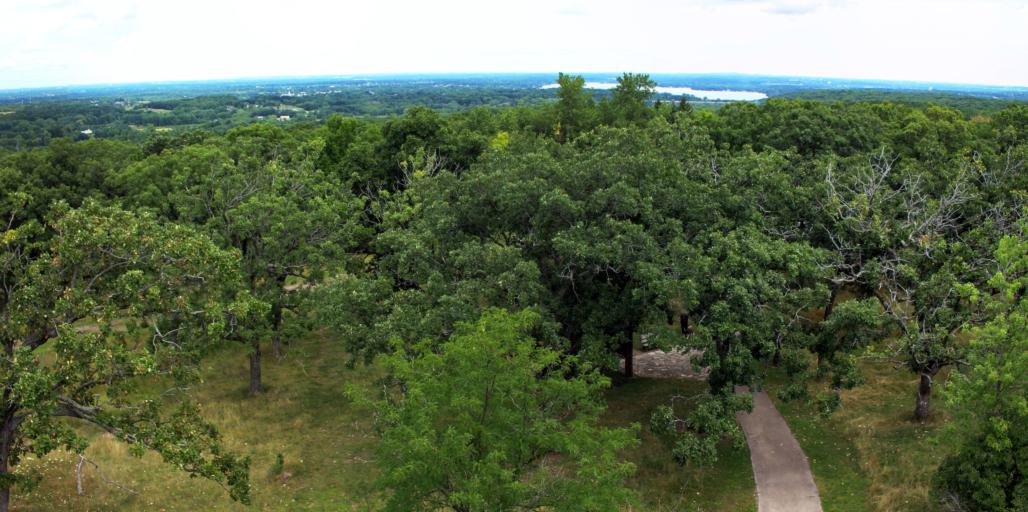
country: US
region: Wisconsin
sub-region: Waukesha County
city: Delafield
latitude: 43.0325
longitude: -88.3928
